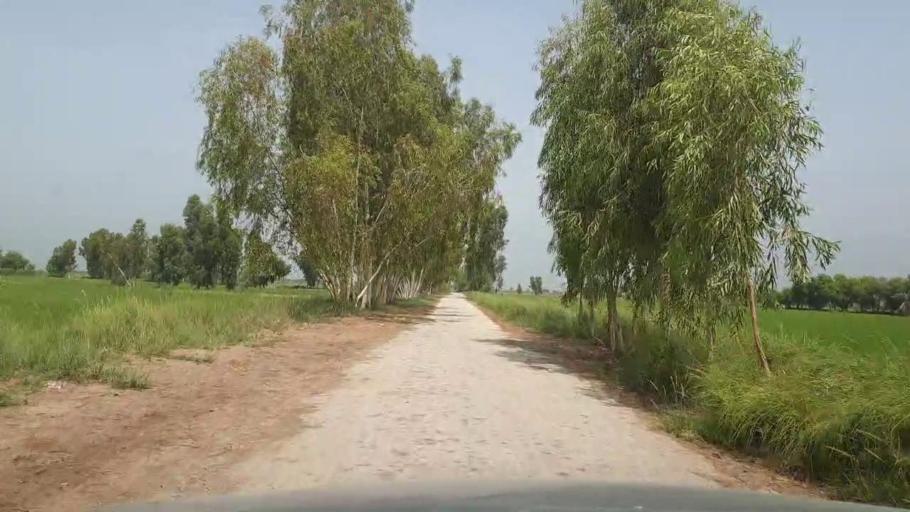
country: PK
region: Sindh
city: Garhi Yasin
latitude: 27.9470
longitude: 68.3689
